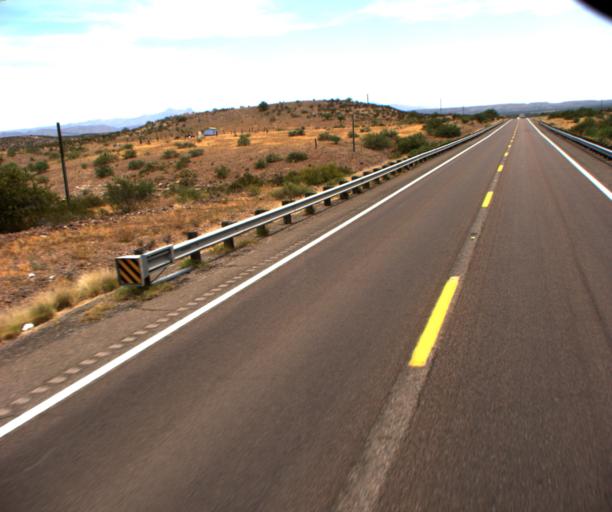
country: US
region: Arizona
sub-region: Graham County
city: Bylas
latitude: 33.1993
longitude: -110.1861
